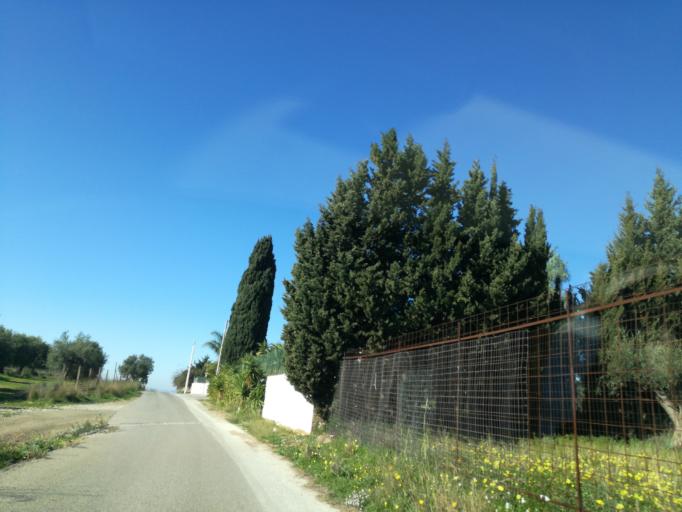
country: IT
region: Sicily
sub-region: Provincia di Caltanissetta
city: Niscemi
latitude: 37.0600
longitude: 14.3537
